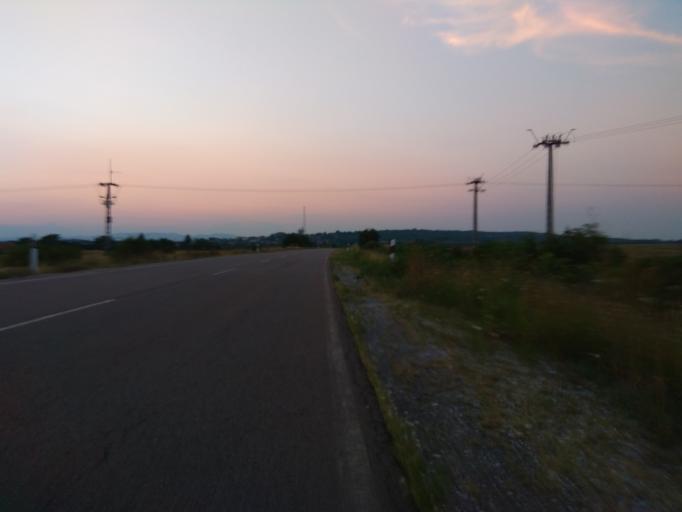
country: HU
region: Borsod-Abauj-Zemplen
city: Emod
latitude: 47.9289
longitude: 20.8322
